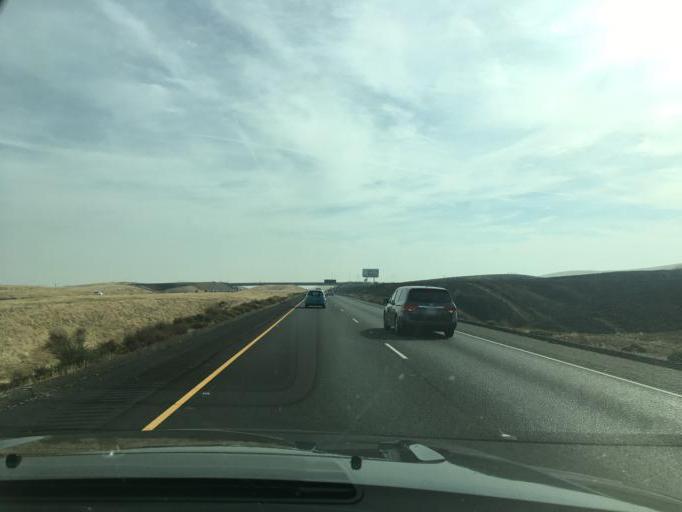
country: US
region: California
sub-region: Kings County
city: Kettleman City
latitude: 36.0117
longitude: -119.9939
